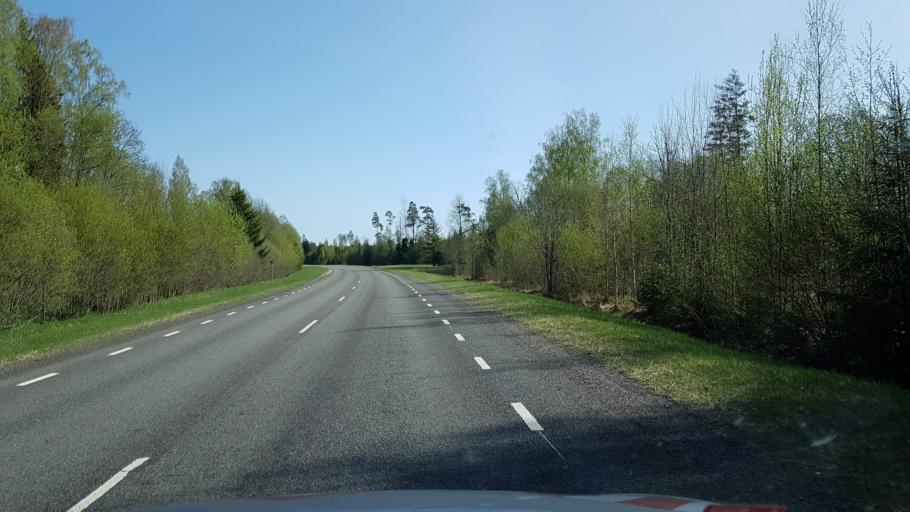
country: EE
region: Viljandimaa
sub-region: Karksi vald
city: Karksi-Nuia
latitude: 58.2188
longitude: 25.5648
